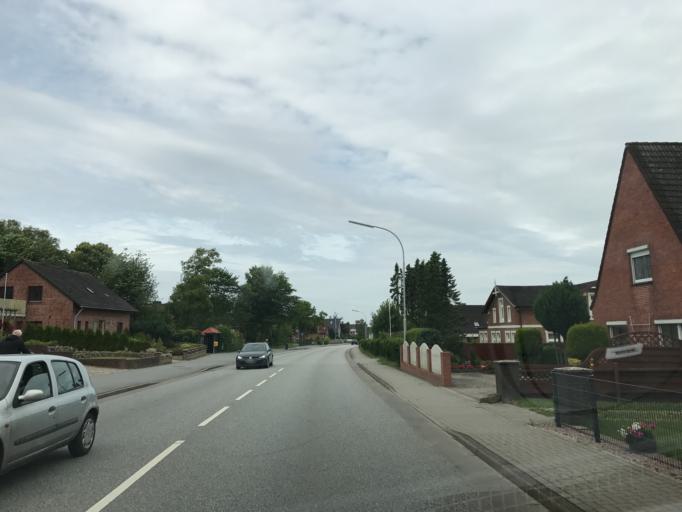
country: DE
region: Schleswig-Holstein
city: Nindorf
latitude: 54.0877
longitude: 9.1025
